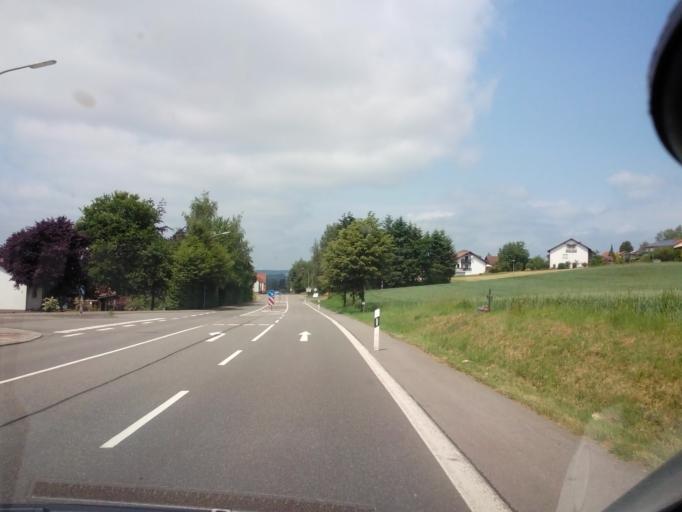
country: DE
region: Saarland
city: Eppelborn
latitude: 49.4017
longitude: 6.9777
